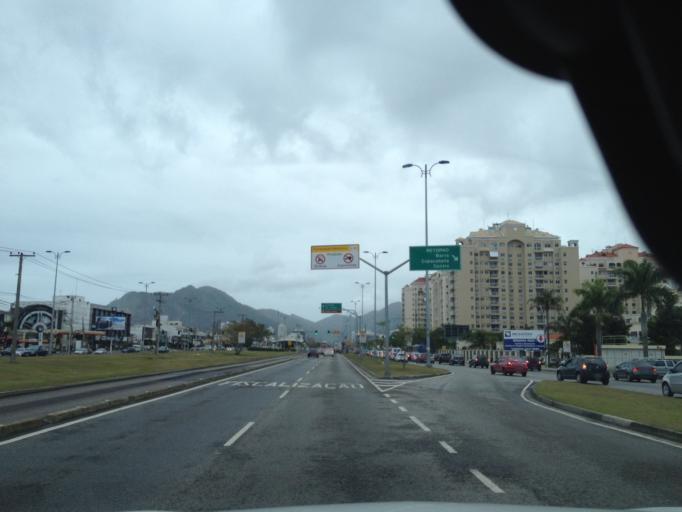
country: BR
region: Rio de Janeiro
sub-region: Nilopolis
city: Nilopolis
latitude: -23.0147
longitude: -43.4687
